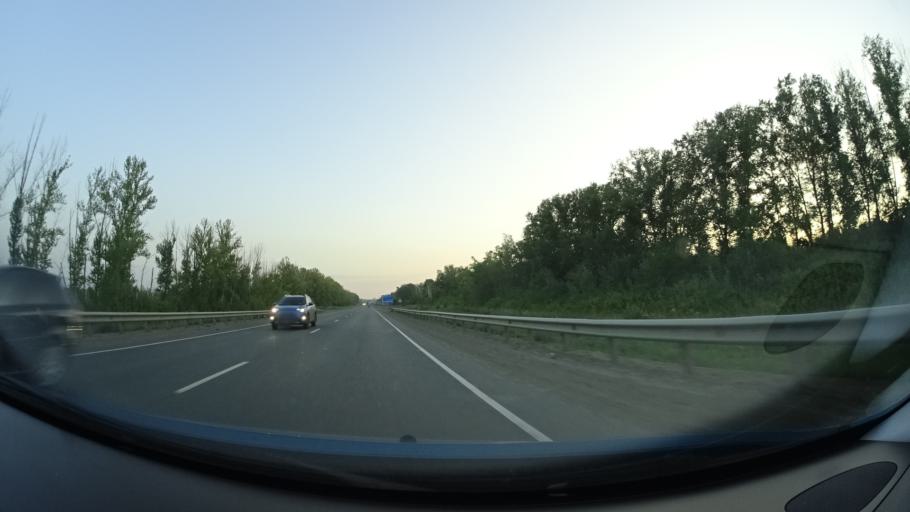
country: RU
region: Samara
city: Sukhodol
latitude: 53.8753
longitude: 51.2154
